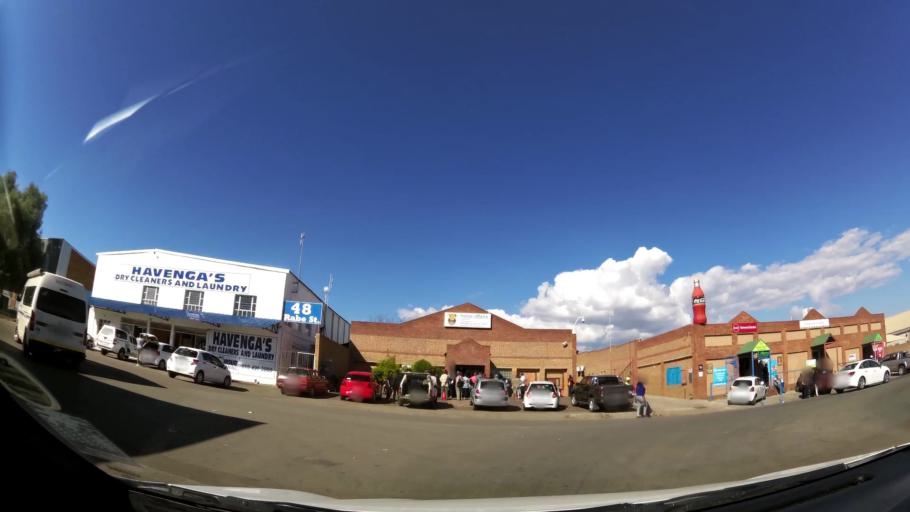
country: ZA
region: Limpopo
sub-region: Waterberg District Municipality
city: Mokopane
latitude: -24.1822
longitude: 29.0177
